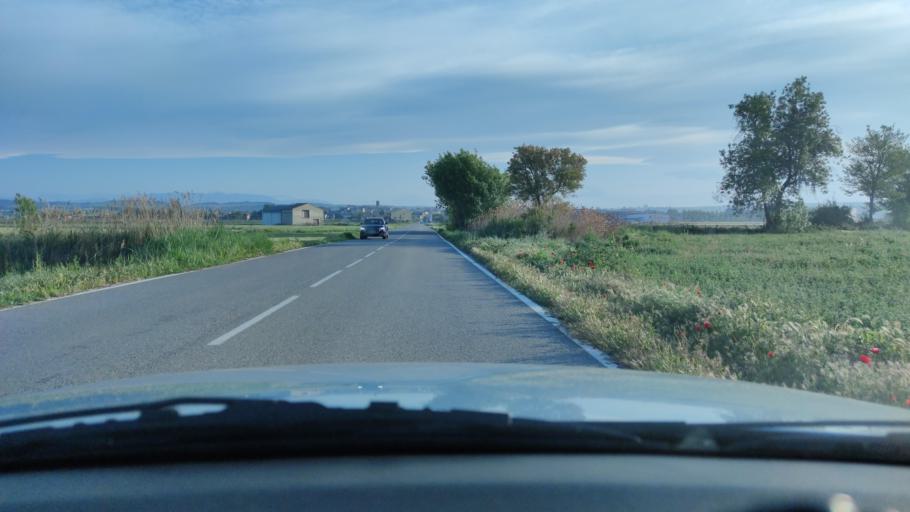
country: ES
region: Catalonia
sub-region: Provincia de Lleida
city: Castellsera
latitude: 41.7373
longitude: 0.9848
